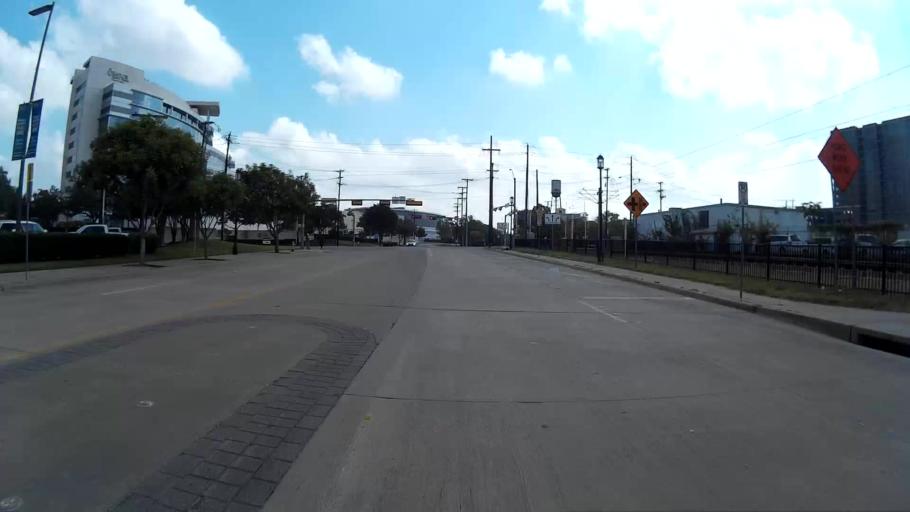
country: US
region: Texas
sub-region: Dallas County
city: Dallas
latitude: 32.7869
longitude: -96.7803
